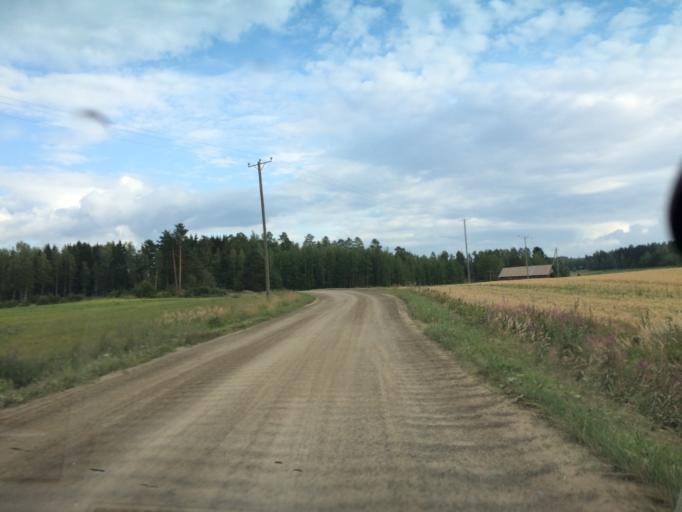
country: FI
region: Pirkanmaa
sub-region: Tampere
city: Luopioinen
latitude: 61.2638
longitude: 24.7003
